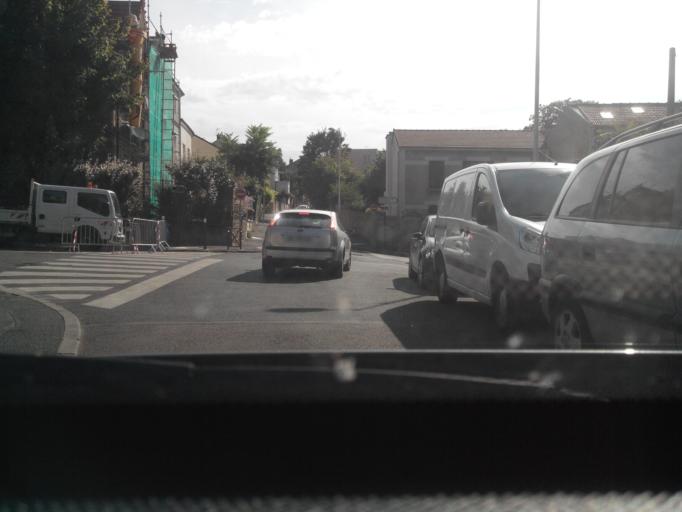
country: FR
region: Ile-de-France
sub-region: Departement du Val-de-Marne
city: Cachan
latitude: 48.7935
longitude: 2.3402
